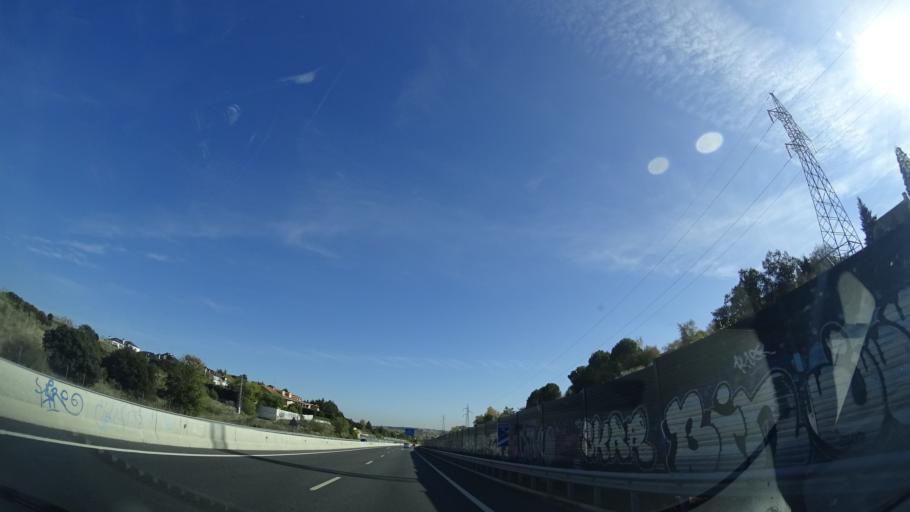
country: ES
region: Madrid
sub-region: Provincia de Madrid
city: Villanueva del Pardillo
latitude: 40.4896
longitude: -3.9510
